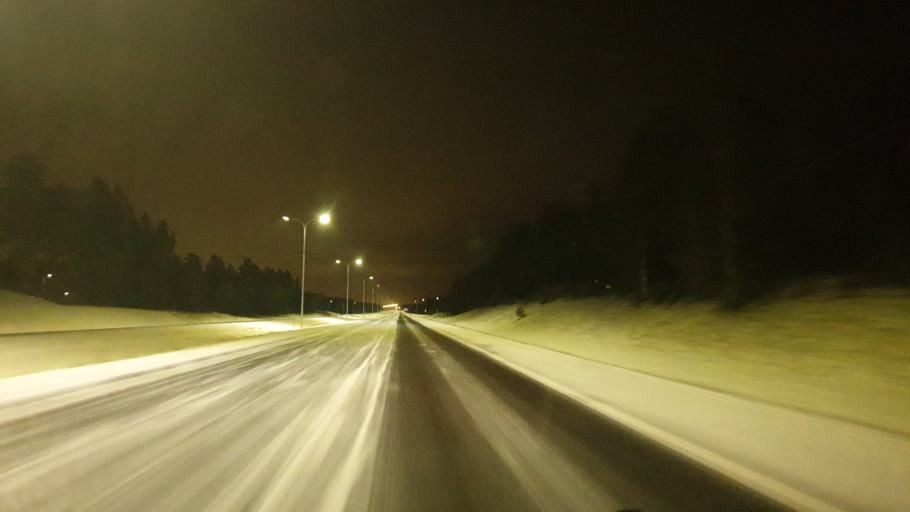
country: FI
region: Northern Ostrobothnia
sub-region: Oulu
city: Haukipudas
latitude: 65.1312
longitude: 25.4322
